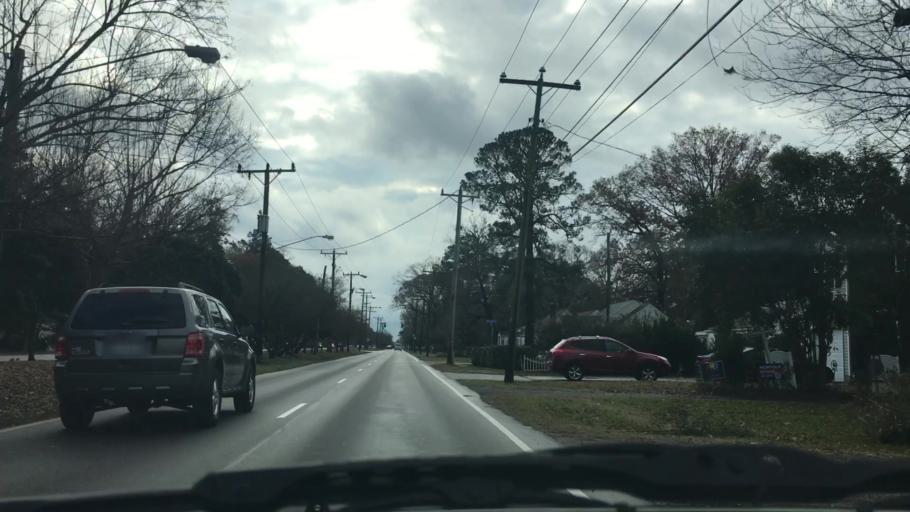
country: US
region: Virginia
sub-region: City of Norfolk
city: Norfolk
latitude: 36.9254
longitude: -76.2433
